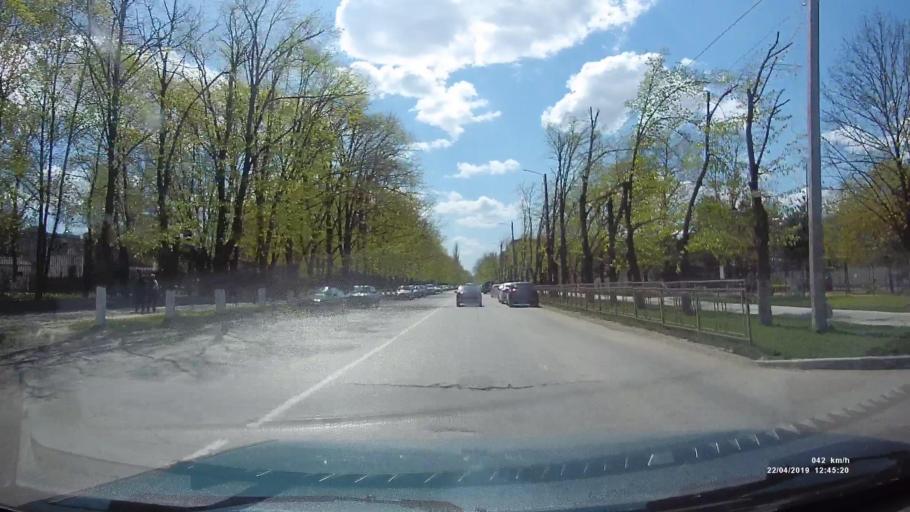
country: RU
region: Rostov
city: Azov
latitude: 47.1043
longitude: 39.4148
